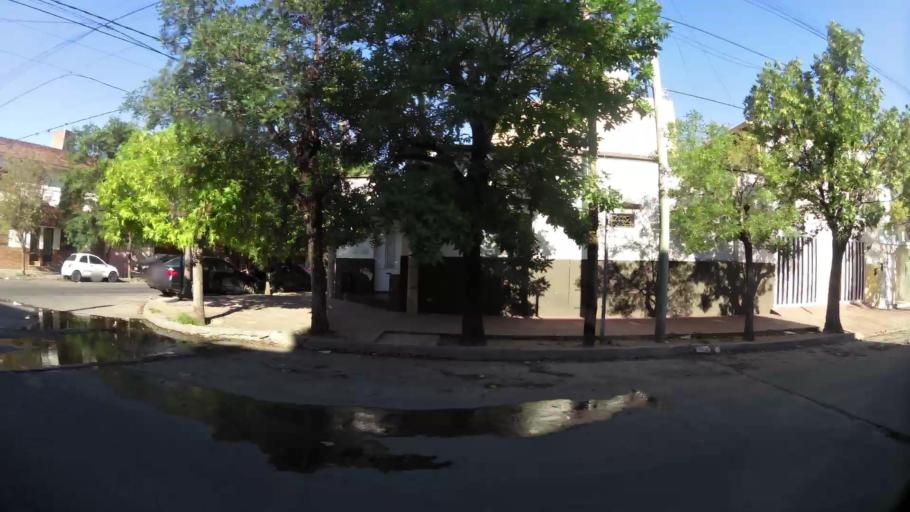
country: AR
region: Cordoba
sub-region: Departamento de Capital
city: Cordoba
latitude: -31.3925
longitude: -64.1770
